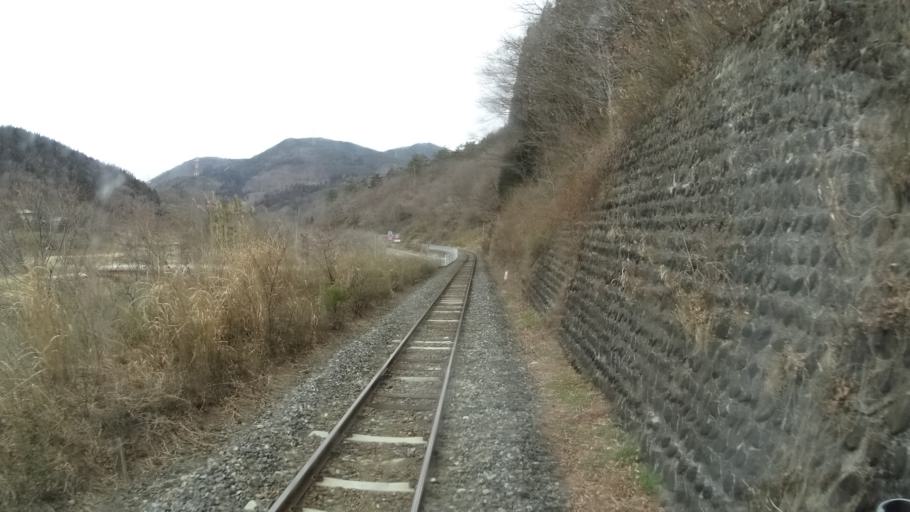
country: JP
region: Iwate
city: Hanamaki
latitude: 39.3587
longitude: 141.3078
